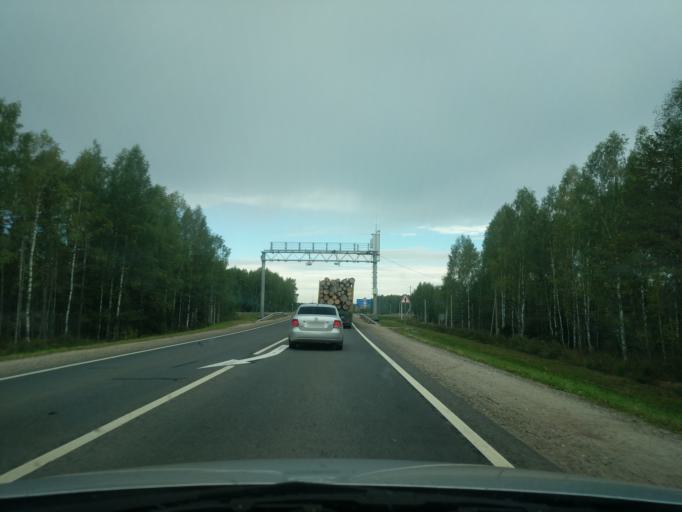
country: RU
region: Kostroma
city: Ostrovskoye
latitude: 57.8080
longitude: 42.2930
